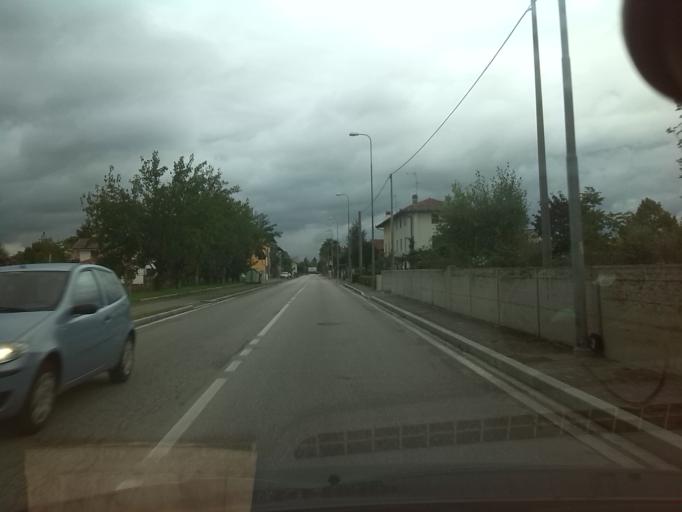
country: IT
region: Friuli Venezia Giulia
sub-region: Provincia di Udine
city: Udine
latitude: 46.0817
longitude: 13.2744
